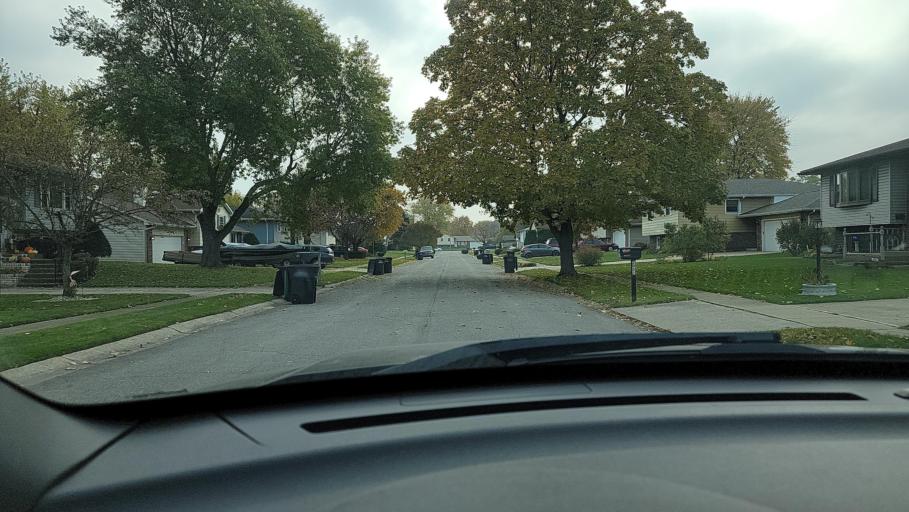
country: US
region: Indiana
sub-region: Porter County
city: Portage
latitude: 41.5919
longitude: -87.1569
